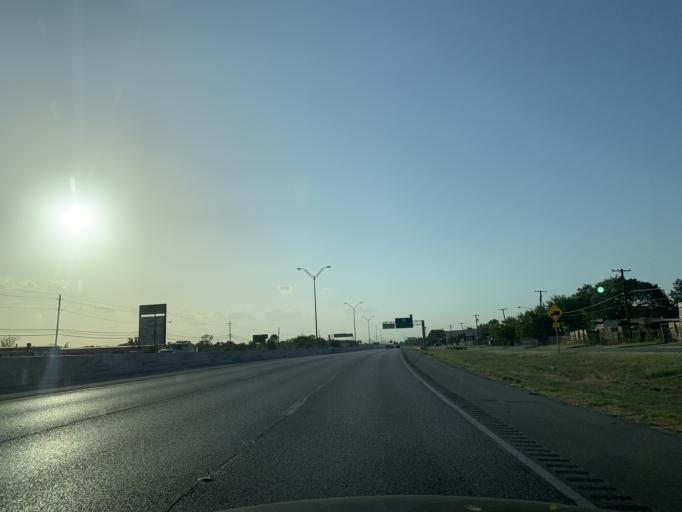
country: US
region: Texas
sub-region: Dallas County
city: Balch Springs
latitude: 32.7061
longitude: -96.6724
